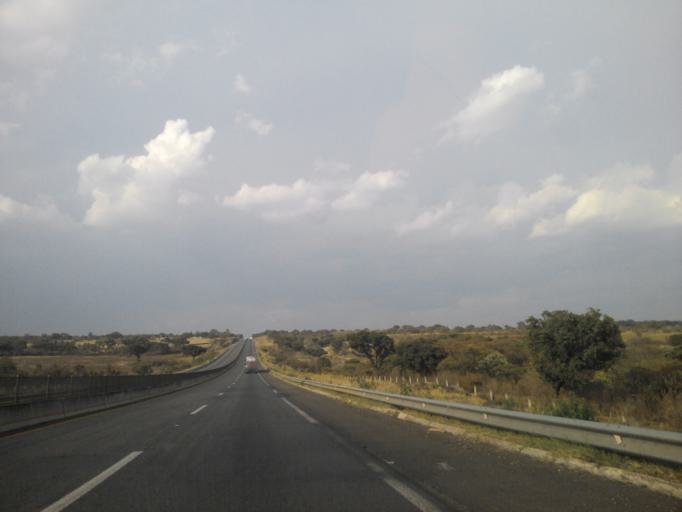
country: MX
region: Jalisco
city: Tepatitlan de Morelos
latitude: 20.8461
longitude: -102.7813
